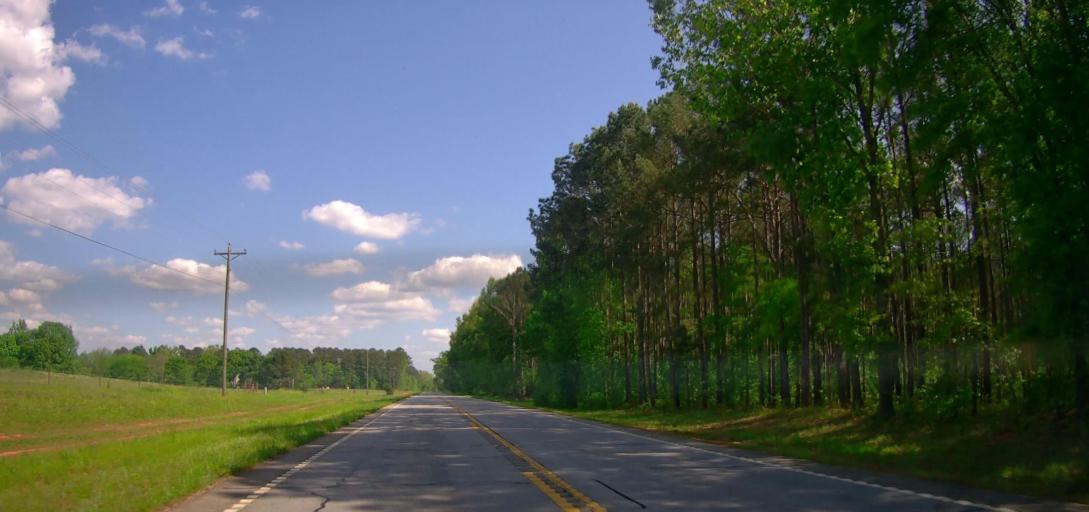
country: US
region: Georgia
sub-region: Greene County
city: Greensboro
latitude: 33.5911
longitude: -83.2883
